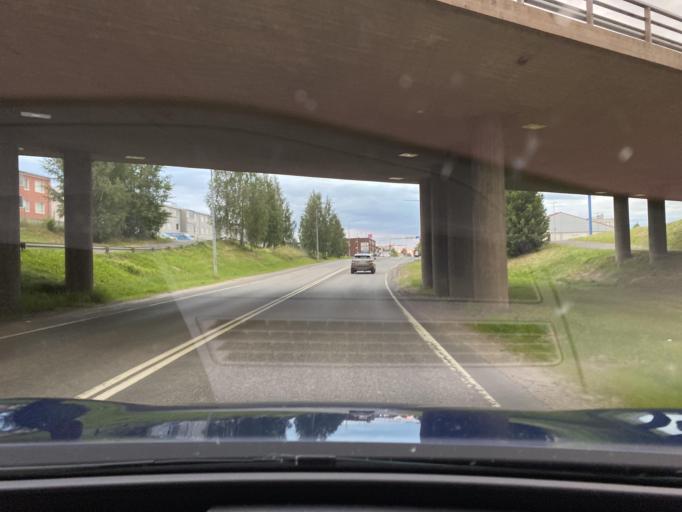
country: FI
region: Northern Ostrobothnia
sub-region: Raahe
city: Raahe
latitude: 64.6814
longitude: 24.4801
